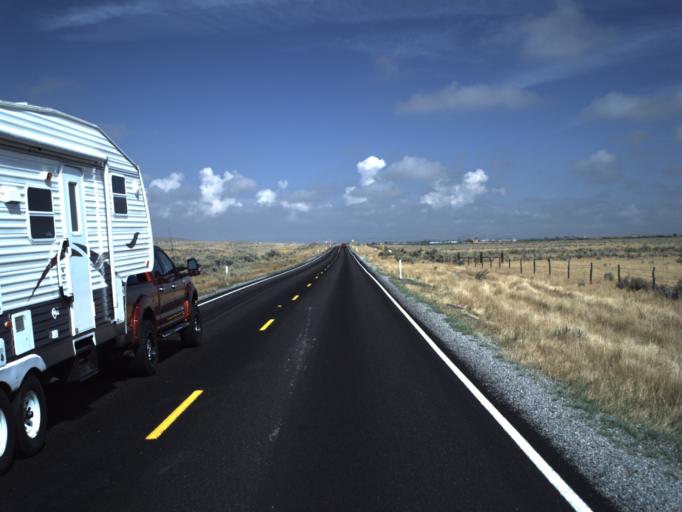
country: US
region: Utah
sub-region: Rich County
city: Randolph
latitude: 41.5682
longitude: -111.1602
